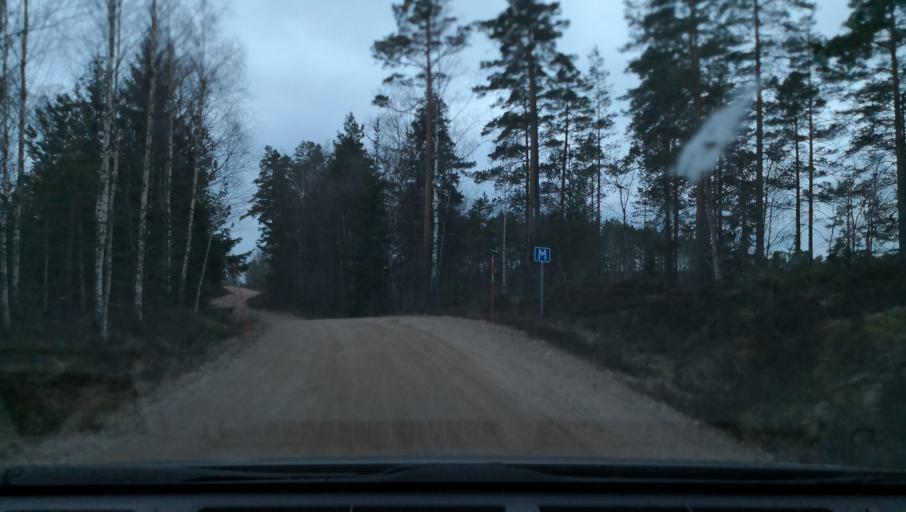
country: SE
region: OErebro
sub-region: Lindesbergs Kommun
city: Fellingsbro
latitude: 59.5979
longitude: 15.5794
